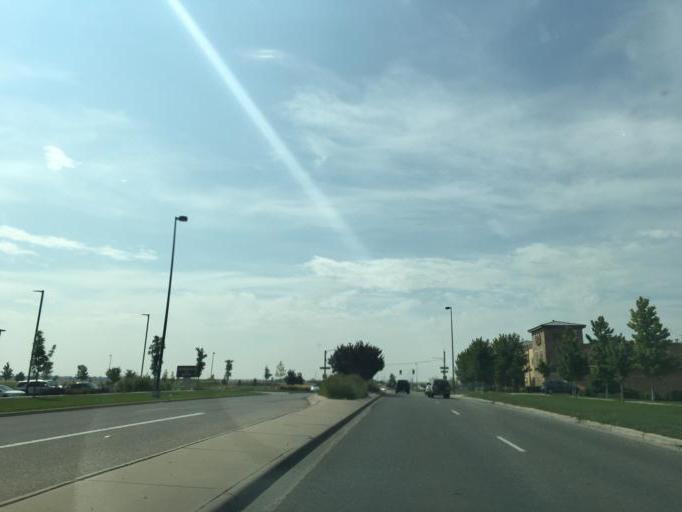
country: US
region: Colorado
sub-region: Adams County
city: Aurora
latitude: 39.8200
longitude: -104.7721
